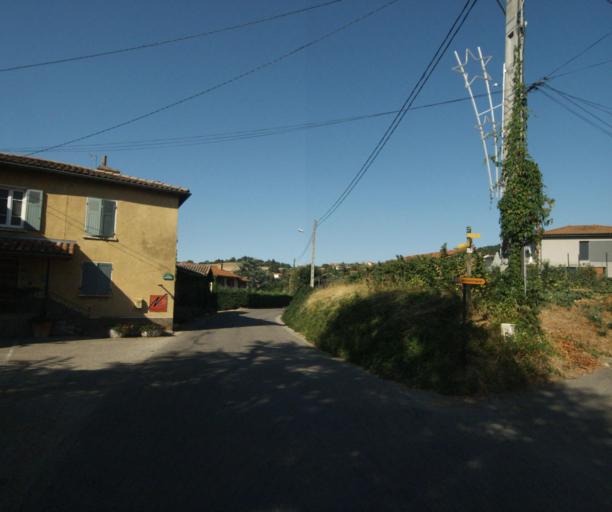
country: FR
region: Rhone-Alpes
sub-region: Departement du Rhone
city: Saint-Pierre-la-Palud
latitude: 45.7800
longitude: 4.6178
